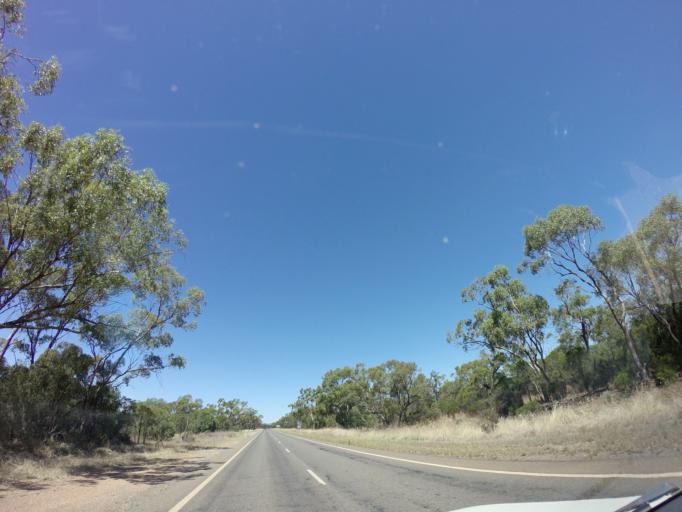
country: AU
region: New South Wales
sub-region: Bogan
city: Nyngan
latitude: -31.5463
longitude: 146.7282
